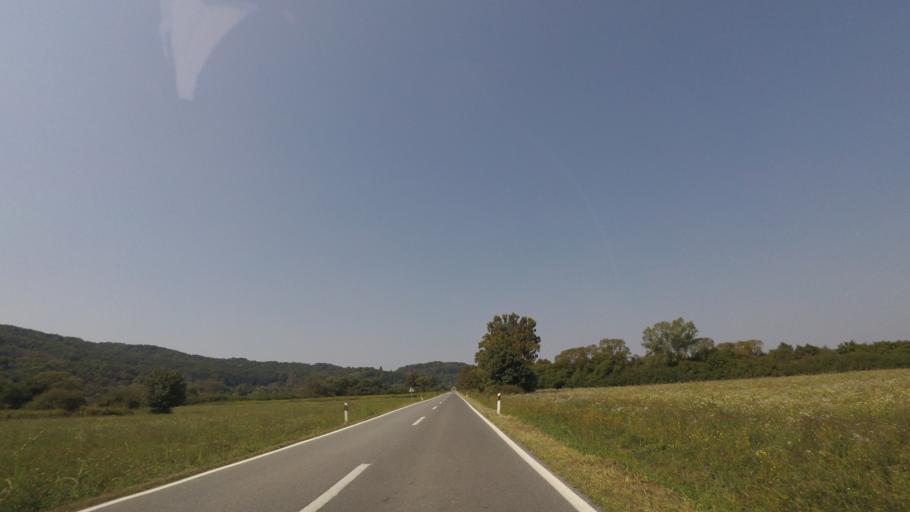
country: HR
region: Pozesko-Slavonska
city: Lipik
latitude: 45.4187
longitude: 17.1205
